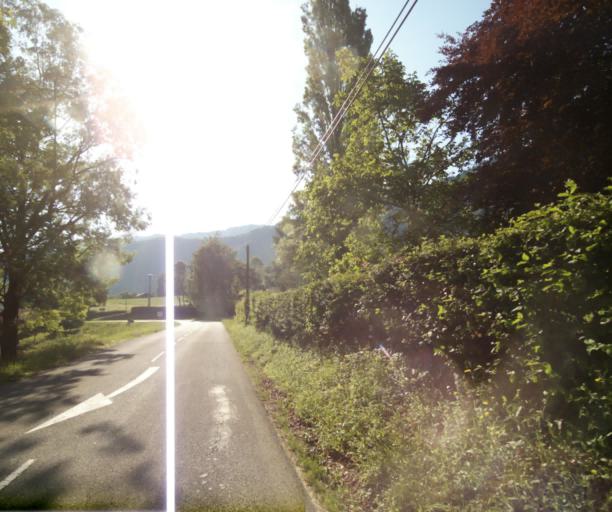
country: FR
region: Rhone-Alpes
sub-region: Departement de la Haute-Savoie
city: Allinges
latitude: 46.3106
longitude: 6.4823
